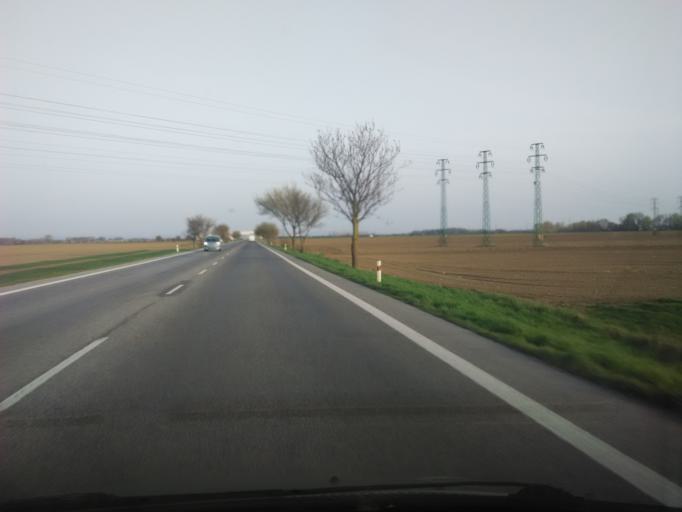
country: SK
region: Nitriansky
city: Sellye
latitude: 48.1738
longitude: 17.8268
